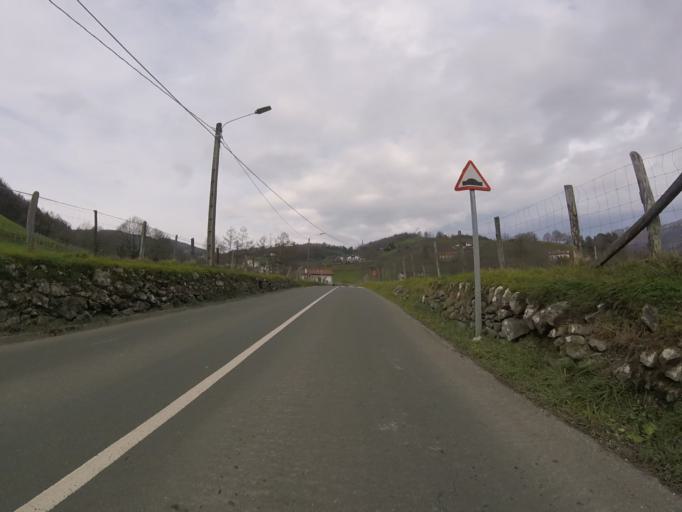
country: ES
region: Basque Country
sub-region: Provincia de Guipuzcoa
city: Errezil
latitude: 43.1397
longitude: -2.1625
